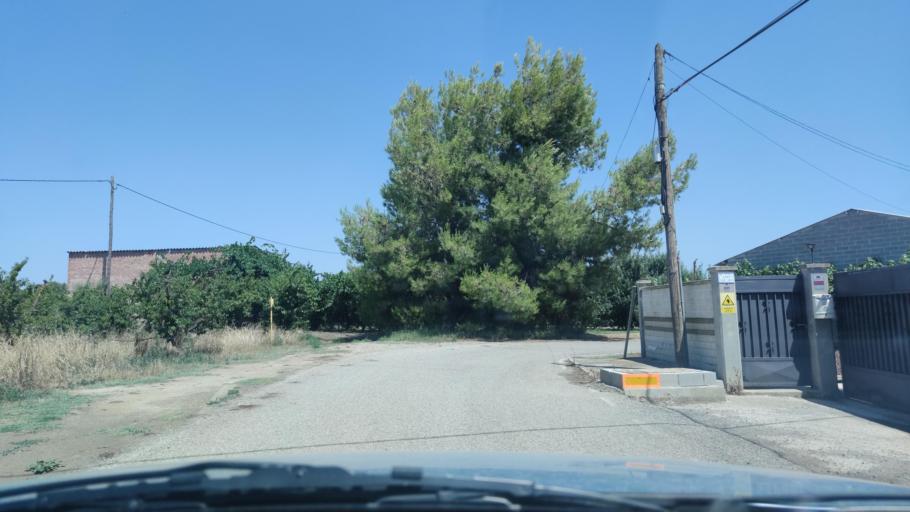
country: ES
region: Catalonia
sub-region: Provincia de Lleida
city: Torrefarrera
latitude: 41.6523
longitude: 0.5907
